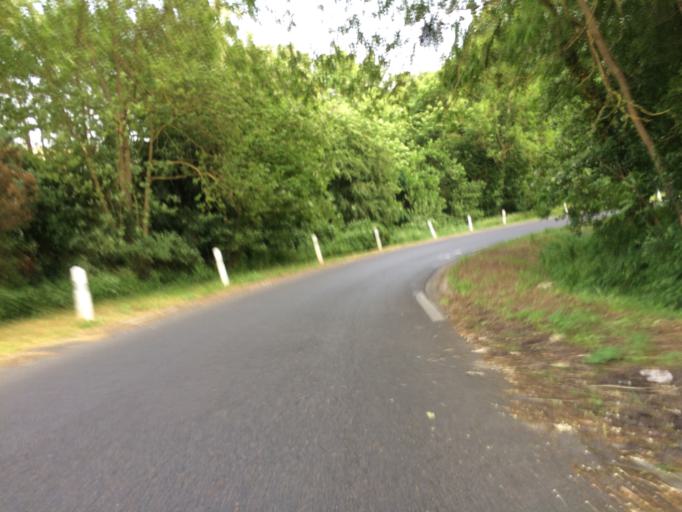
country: FR
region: Ile-de-France
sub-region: Departement de l'Essonne
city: Verrieres-le-Buisson
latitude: 48.7381
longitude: 2.2483
